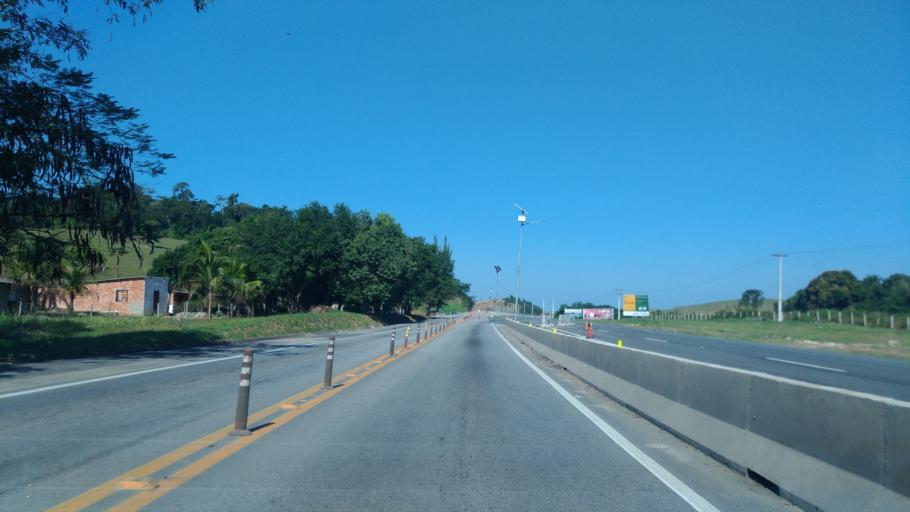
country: BR
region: Rio de Janeiro
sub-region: Macae
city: Macae
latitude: -22.0356
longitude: -41.6937
